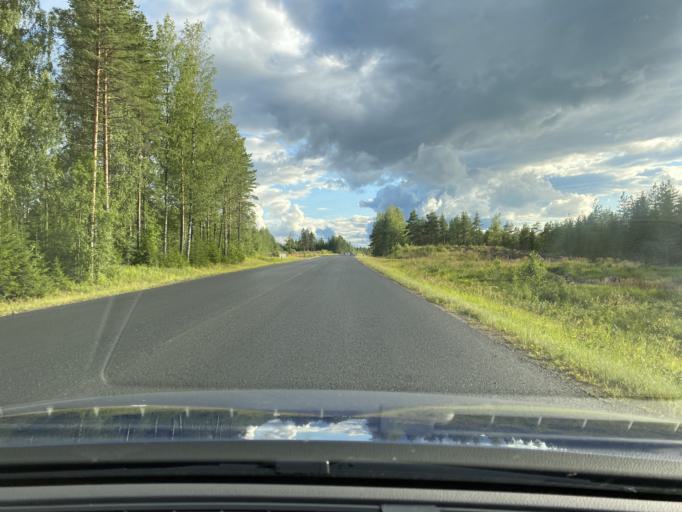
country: FI
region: Haeme
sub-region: Haemeenlinna
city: Renko
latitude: 60.9142
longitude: 24.3225
